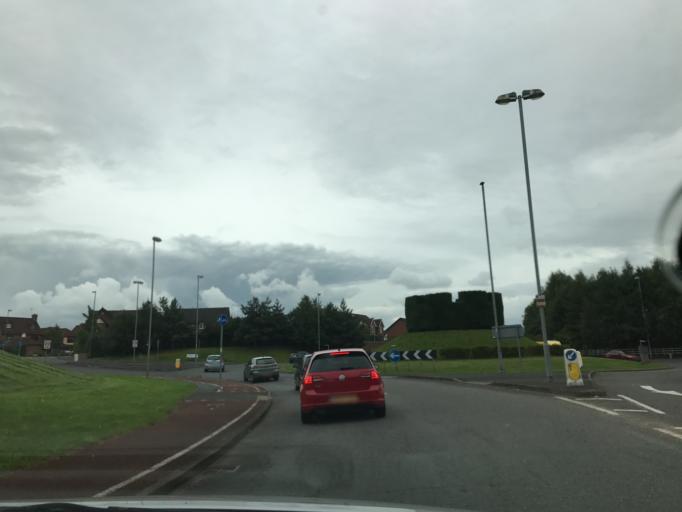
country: GB
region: England
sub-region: Cheshire West and Chester
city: Northwich
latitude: 53.2483
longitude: -2.5143
